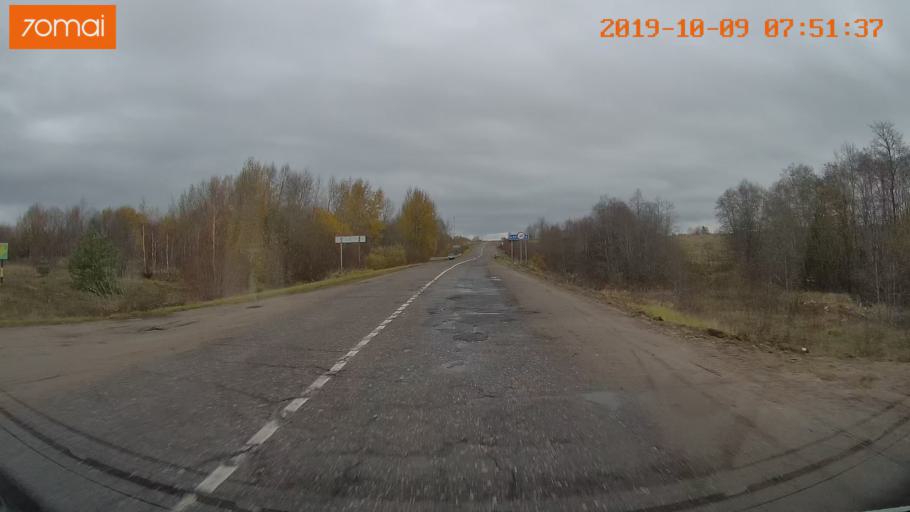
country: RU
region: Jaroslavl
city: Kukoboy
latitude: 58.6845
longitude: 39.8801
